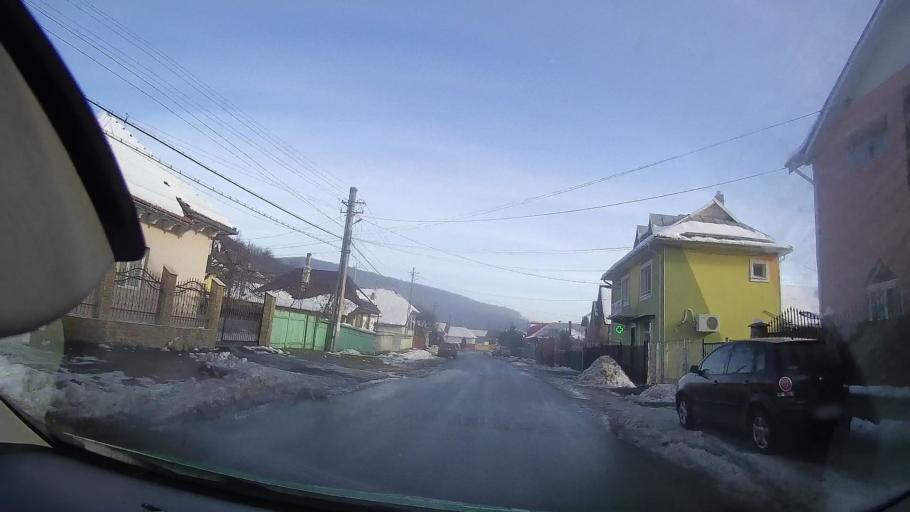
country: RO
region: Neamt
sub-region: Comuna Garcina
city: Garcina
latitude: 46.9768
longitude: 26.3484
